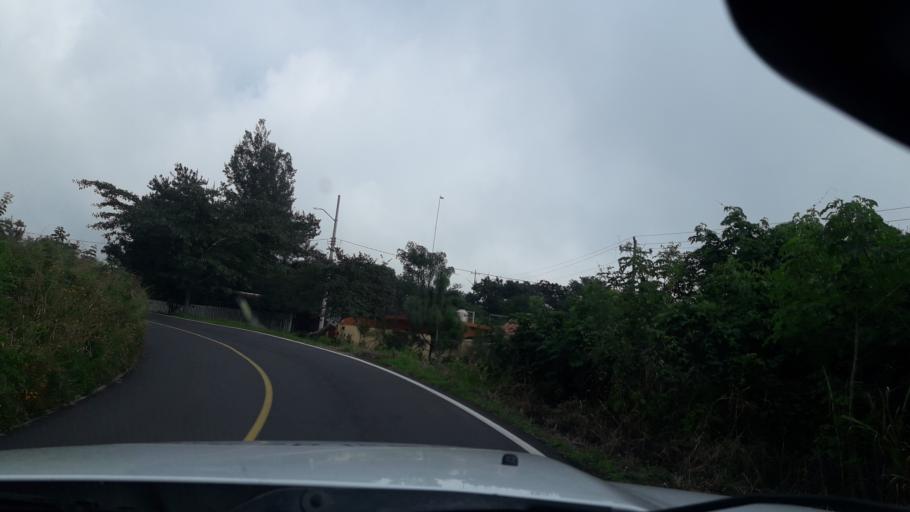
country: MX
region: Colima
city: Suchitlan
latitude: 19.4111
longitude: -103.6534
